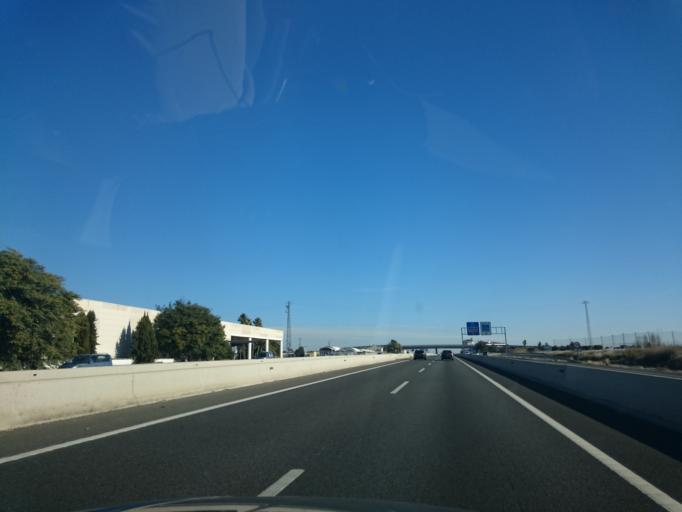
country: ES
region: Catalonia
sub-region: Provincia de Tarragona
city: Cambrils
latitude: 41.0870
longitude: 1.0864
